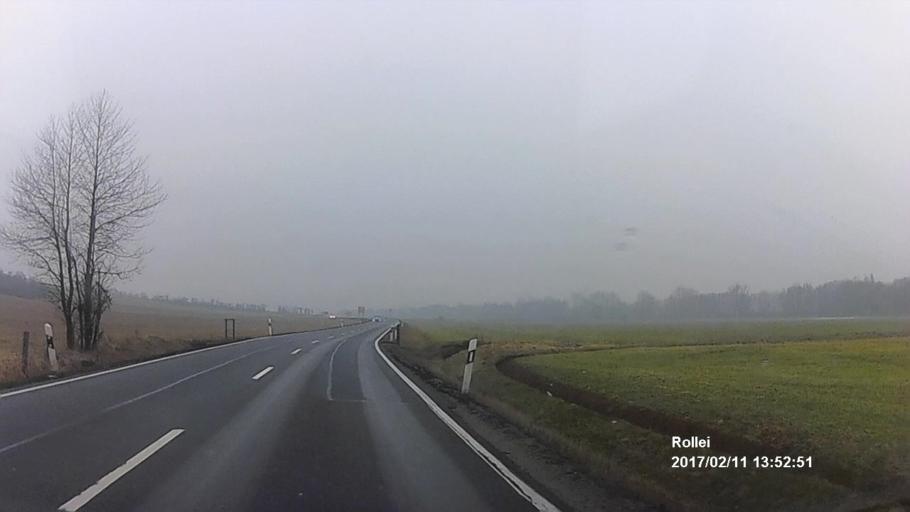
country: DE
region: Thuringia
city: Wipperdorf
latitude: 51.5134
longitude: 10.6878
